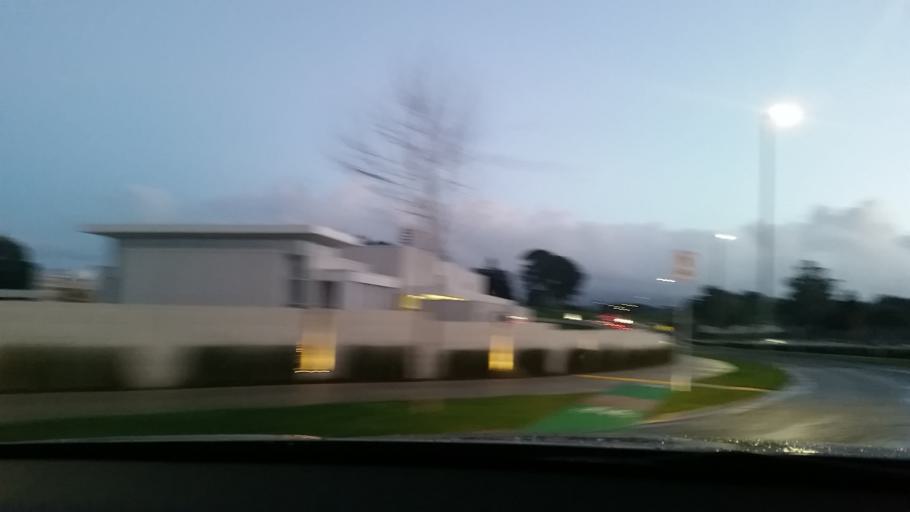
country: NZ
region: Waikato
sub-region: Hamilton City
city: Hamilton
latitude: -37.8222
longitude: 175.2262
